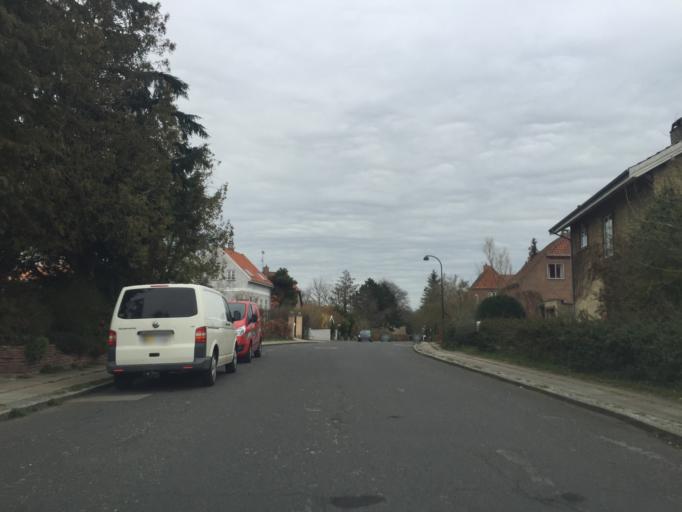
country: DK
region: Capital Region
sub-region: Gentofte Kommune
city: Charlottenlund
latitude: 55.7472
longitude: 12.5460
